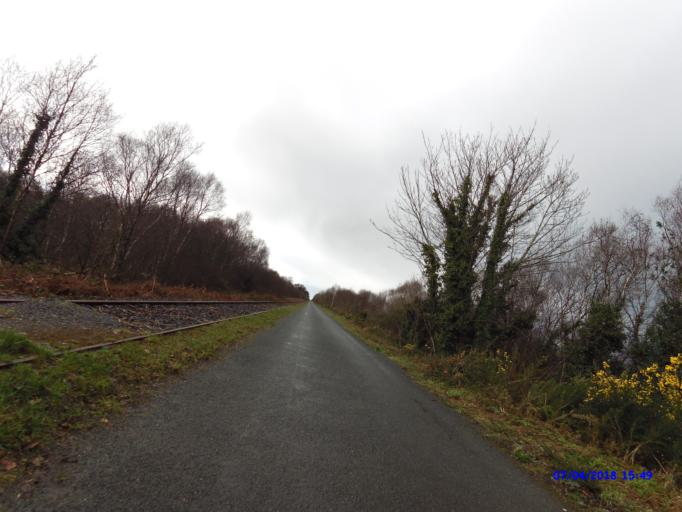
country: IE
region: Leinster
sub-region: An Iarmhi
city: Athlone
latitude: 53.4133
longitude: -7.8490
